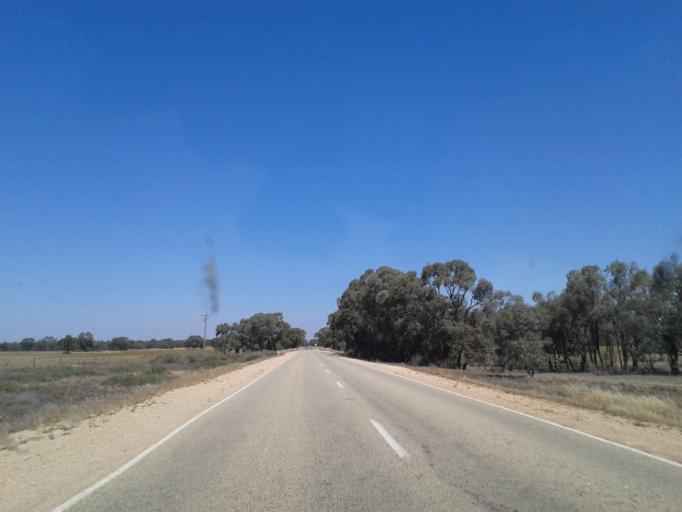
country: AU
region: Victoria
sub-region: Swan Hill
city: Swan Hill
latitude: -35.0148
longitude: 143.3115
